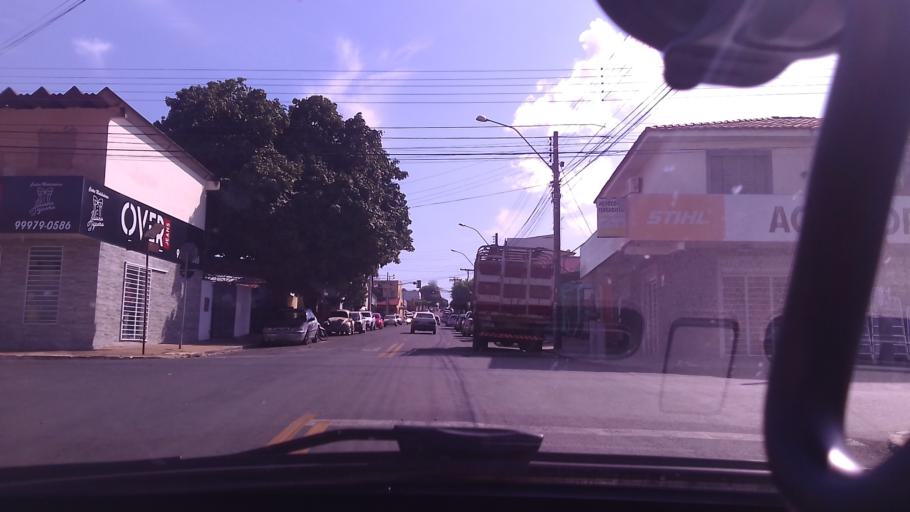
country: BR
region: Goias
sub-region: Mineiros
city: Mineiros
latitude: -17.5641
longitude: -52.5502
